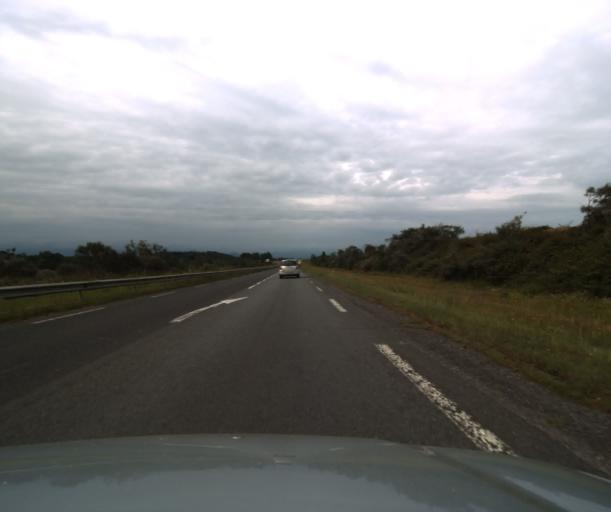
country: FR
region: Midi-Pyrenees
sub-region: Departement des Hautes-Pyrenees
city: Juillan
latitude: 43.2025
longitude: 0.0083
